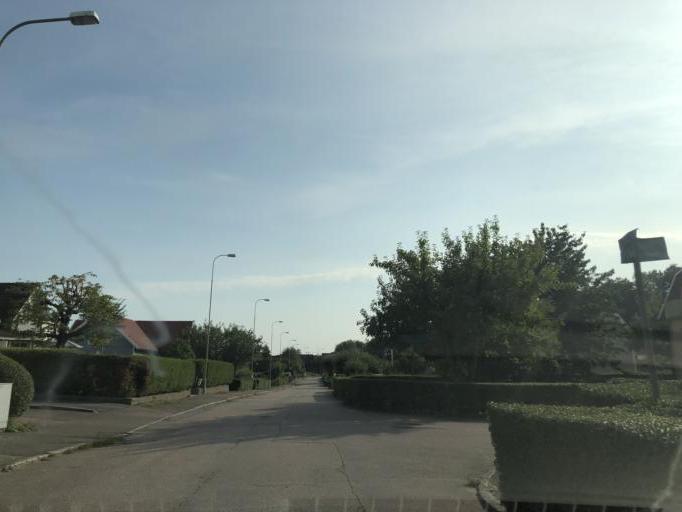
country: SE
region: Vaestra Goetaland
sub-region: Goteborg
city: Goeteborg
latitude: 57.7350
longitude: 11.9830
